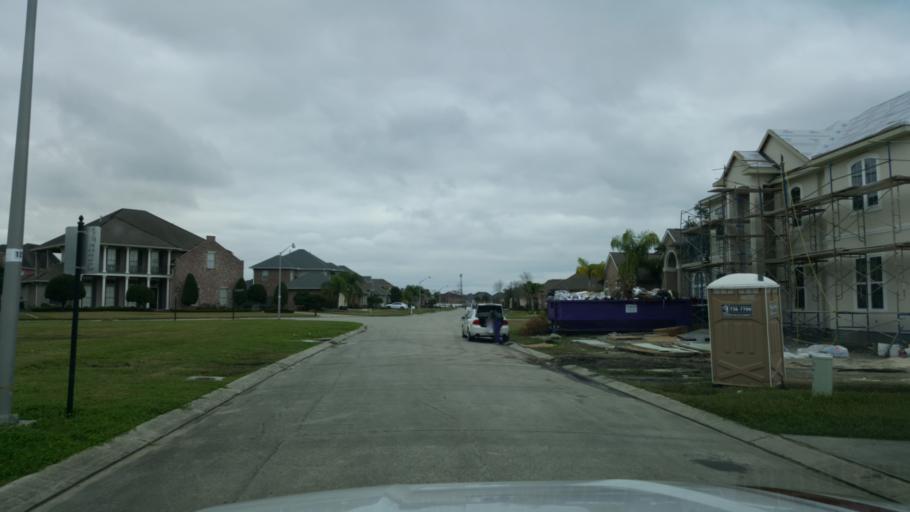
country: US
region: Louisiana
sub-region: Jefferson Parish
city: Woodmere
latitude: 29.8731
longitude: -90.0756
